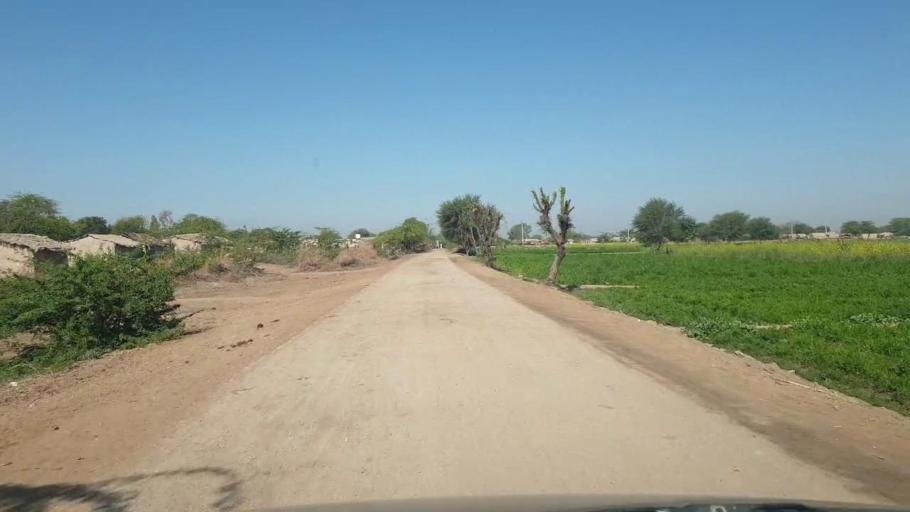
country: PK
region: Sindh
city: Umarkot
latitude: 25.3902
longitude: 69.6971
